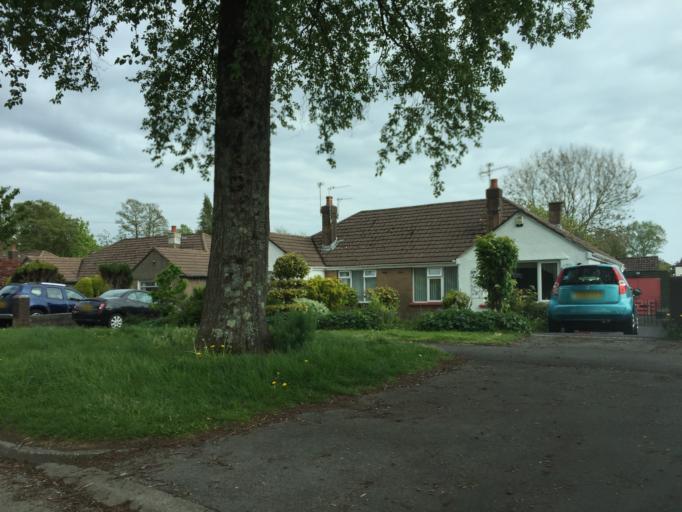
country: GB
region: Wales
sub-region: Cardiff
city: Radyr
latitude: 51.5280
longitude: -3.2148
